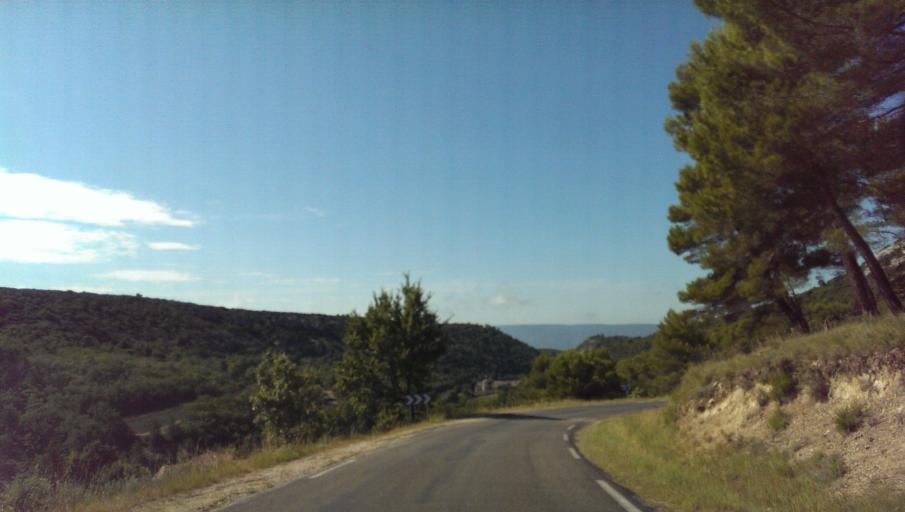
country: FR
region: Provence-Alpes-Cote d'Azur
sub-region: Departement du Vaucluse
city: Gordes
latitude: 43.9375
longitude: 5.1896
